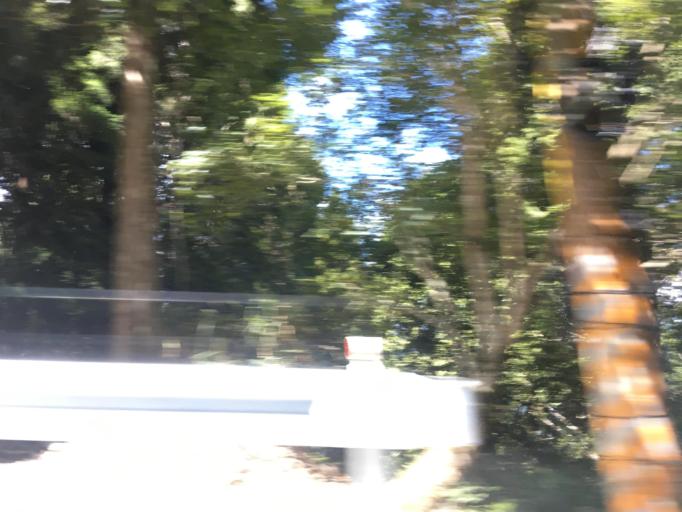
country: TW
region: Taiwan
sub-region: Yilan
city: Yilan
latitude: 24.5058
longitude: 121.5257
